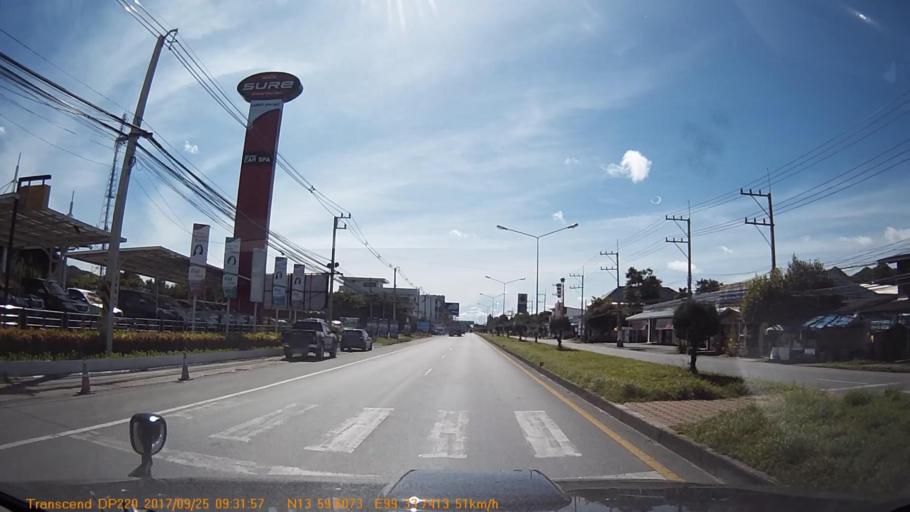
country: TH
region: Kanchanaburi
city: Kanchanaburi
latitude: 13.9933
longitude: 99.5626
